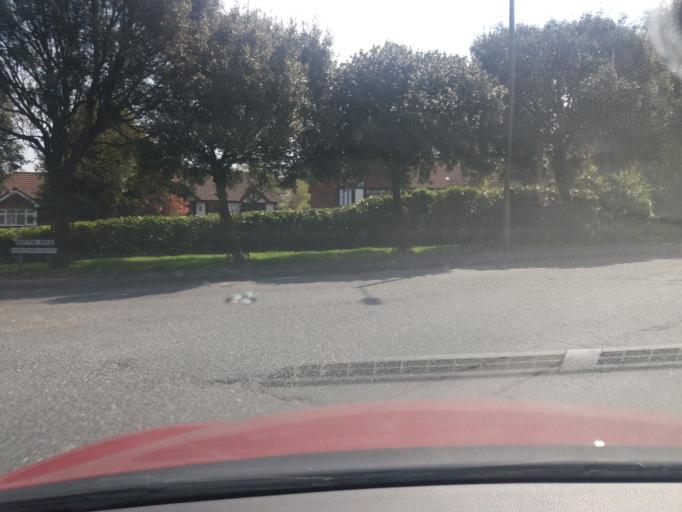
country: GB
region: England
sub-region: Lancashire
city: Chorley
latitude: 53.6778
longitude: -2.6353
